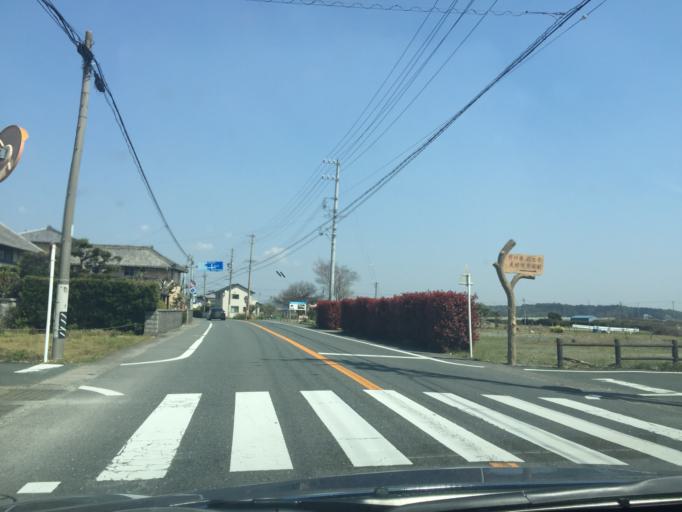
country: JP
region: Shizuoka
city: Kosai-shi
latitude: 34.8007
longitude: 137.6297
